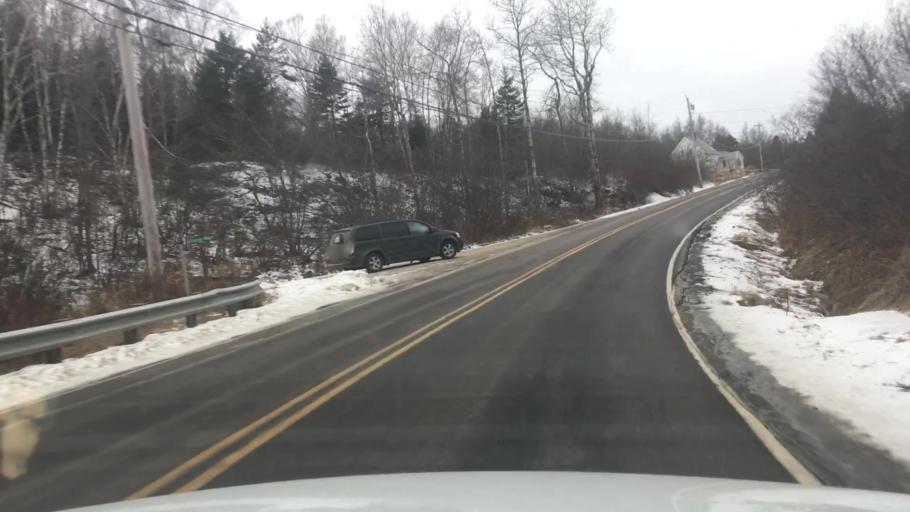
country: US
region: Maine
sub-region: Washington County
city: East Machias
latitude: 44.7252
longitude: -67.3865
